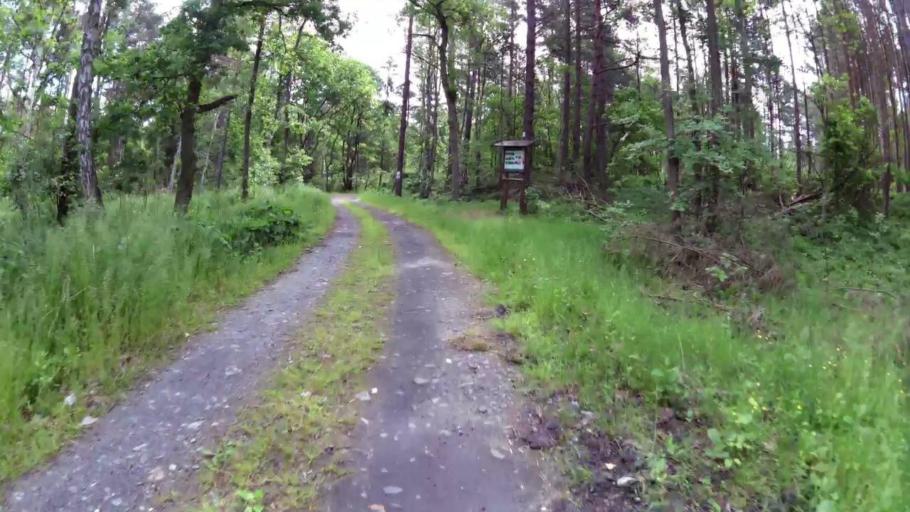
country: PL
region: West Pomeranian Voivodeship
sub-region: Swinoujscie
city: Swinoujscie
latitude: 53.9105
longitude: 14.3084
